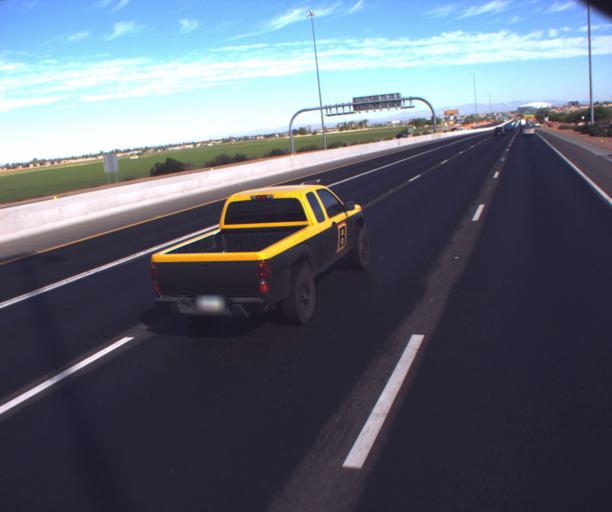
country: US
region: Arizona
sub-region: Maricopa County
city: Tolleson
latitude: 33.4811
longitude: -112.2637
